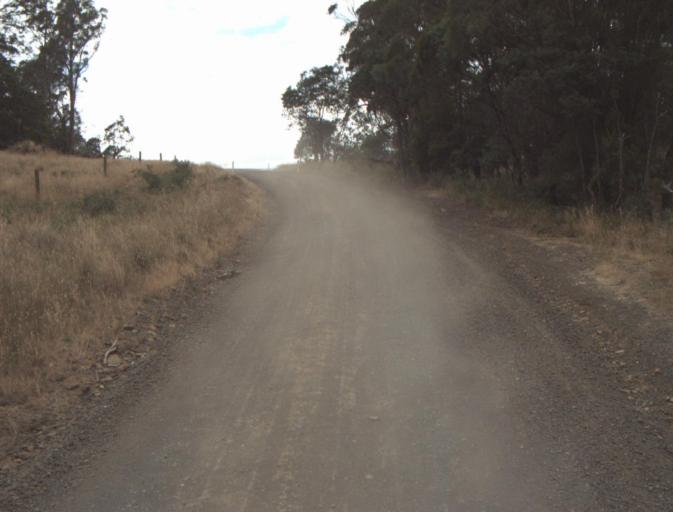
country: AU
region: Tasmania
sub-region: Northern Midlands
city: Evandale
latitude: -41.5204
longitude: 147.3735
